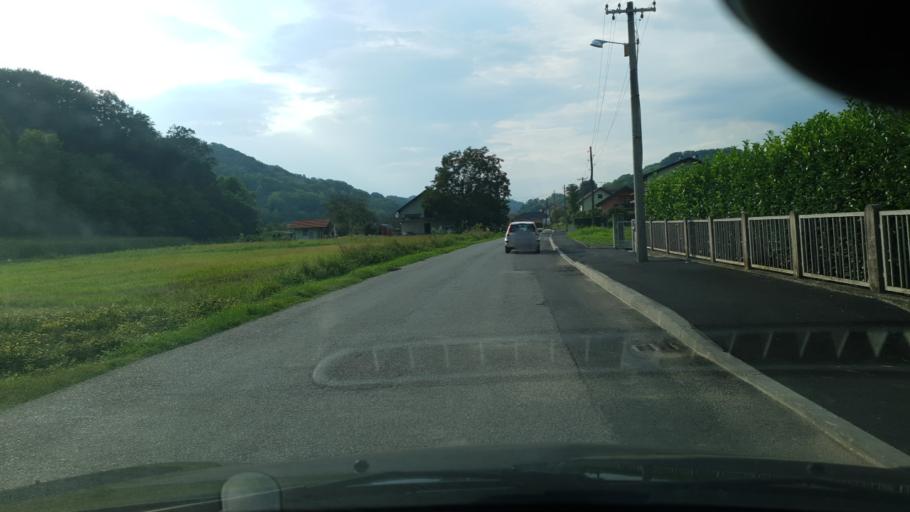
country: HR
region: Krapinsko-Zagorska
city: Zabok
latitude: 46.0806
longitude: 15.8964
